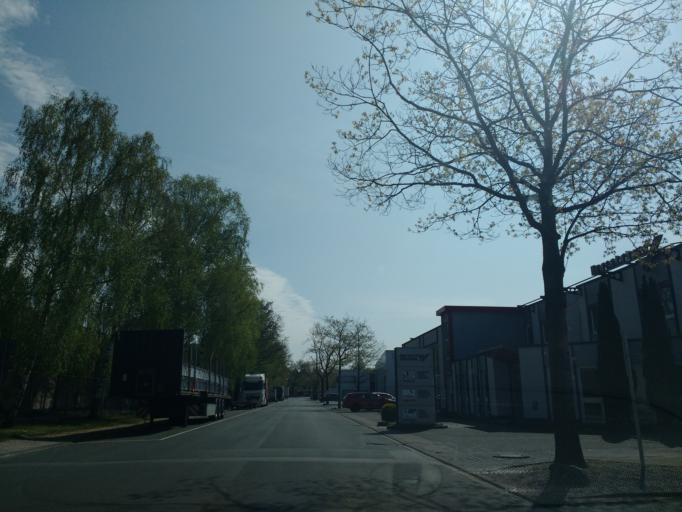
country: DE
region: North Rhine-Westphalia
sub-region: Regierungsbezirk Detmold
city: Hovelhof
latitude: 51.8314
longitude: 8.6499
